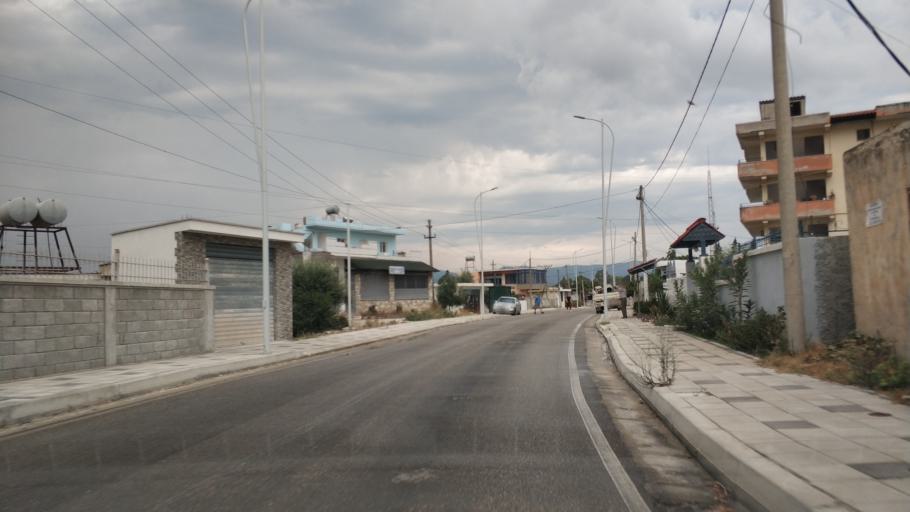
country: AL
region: Vlore
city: Vlore
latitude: 40.4760
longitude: 19.4670
